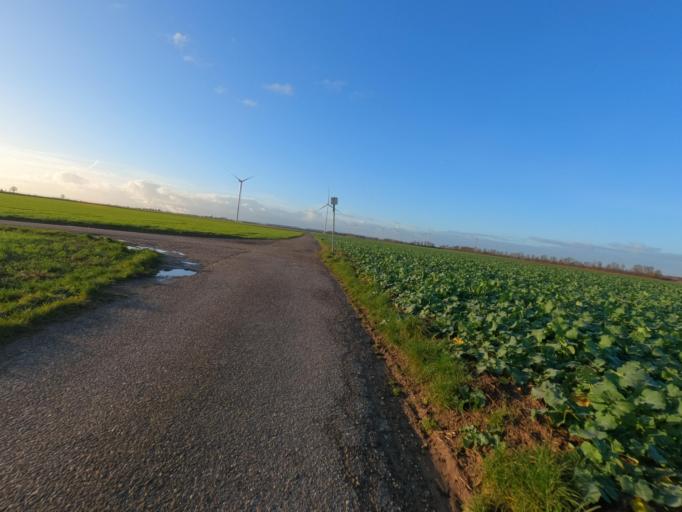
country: DE
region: North Rhine-Westphalia
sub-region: Regierungsbezirk Koln
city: Titz
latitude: 50.9832
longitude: 6.3877
